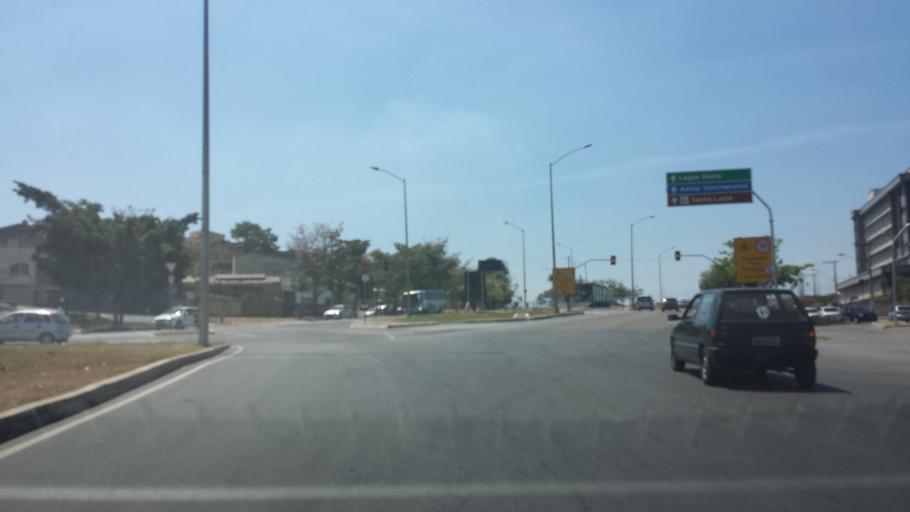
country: BR
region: Minas Gerais
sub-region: Belo Horizonte
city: Belo Horizonte
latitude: -19.8187
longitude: -43.9502
